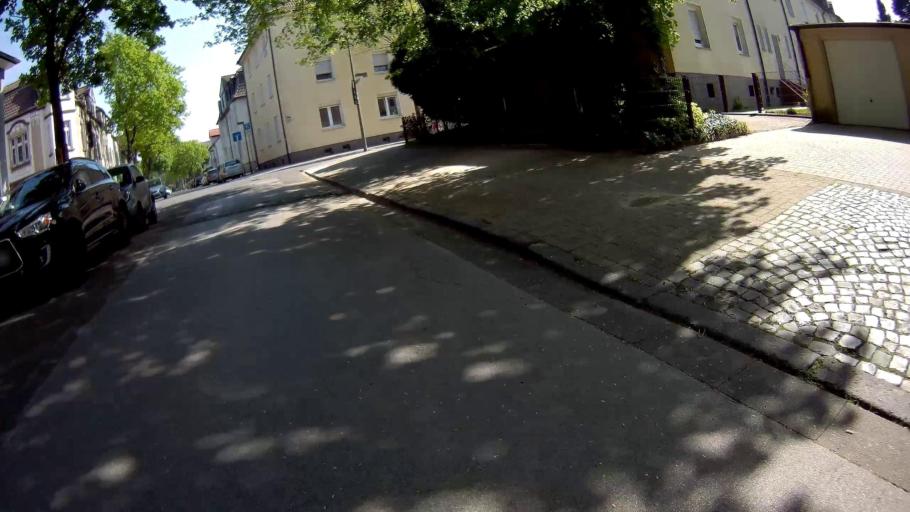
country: DE
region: North Rhine-Westphalia
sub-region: Regierungsbezirk Munster
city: Gladbeck
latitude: 51.5827
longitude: 7.0573
